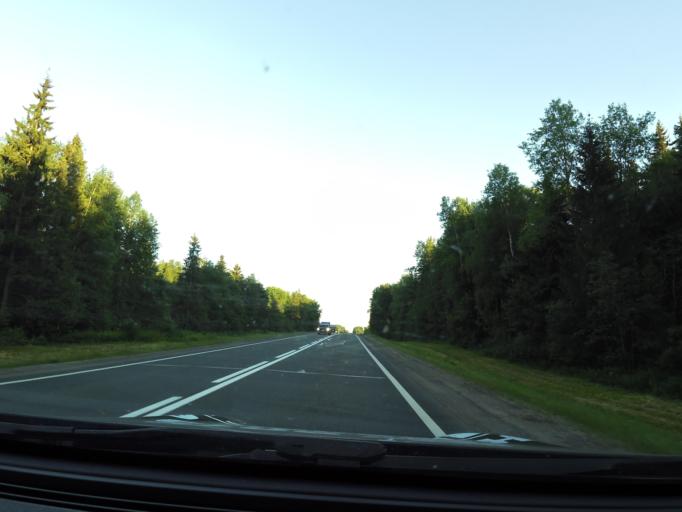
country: RU
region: Vologda
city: Gryazovets
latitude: 58.6878
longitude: 40.3036
